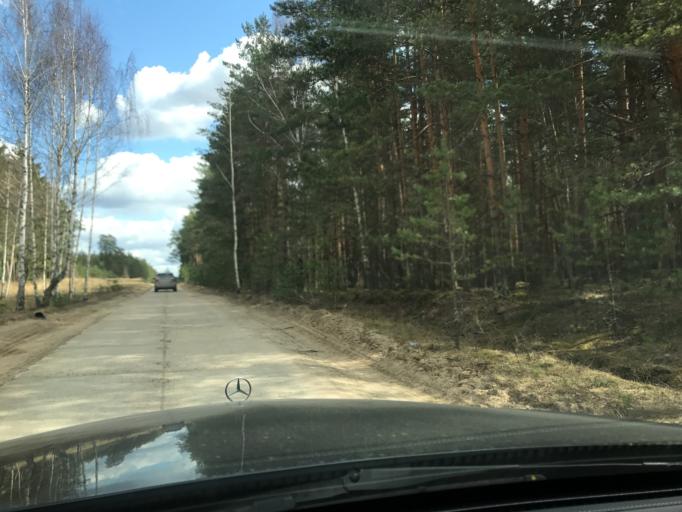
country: RU
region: Vladimir
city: Pokrov
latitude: 55.8613
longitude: 39.2073
